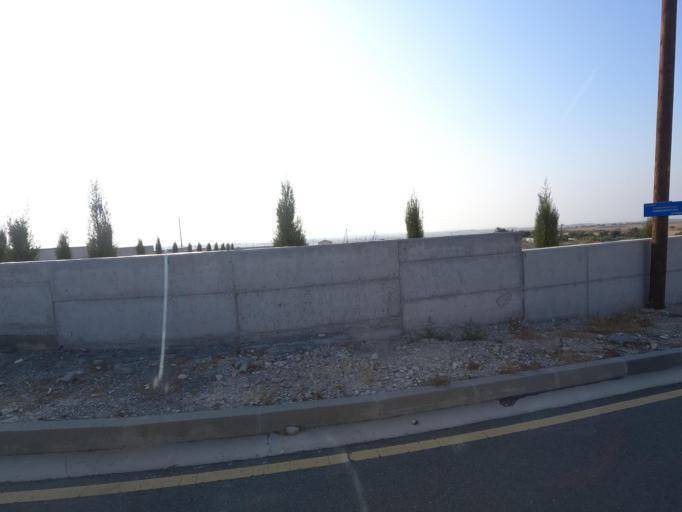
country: CY
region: Larnaka
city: Tersefanou
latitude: 34.8366
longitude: 33.5138
